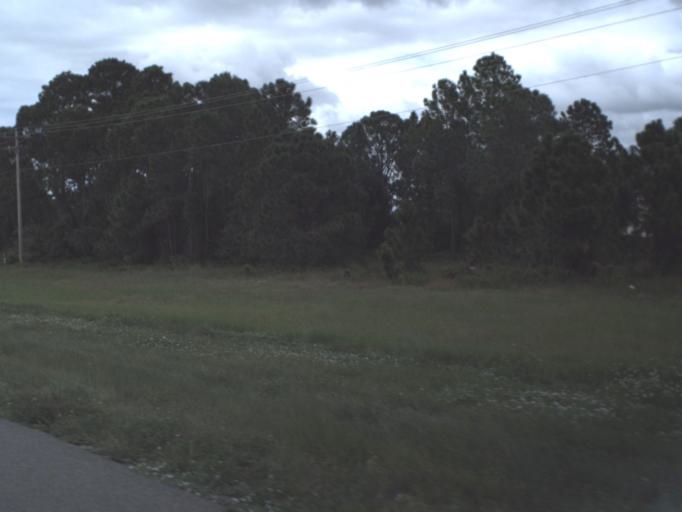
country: US
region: Florida
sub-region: Lee County
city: Lehigh Acres
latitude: 26.5221
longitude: -81.5782
